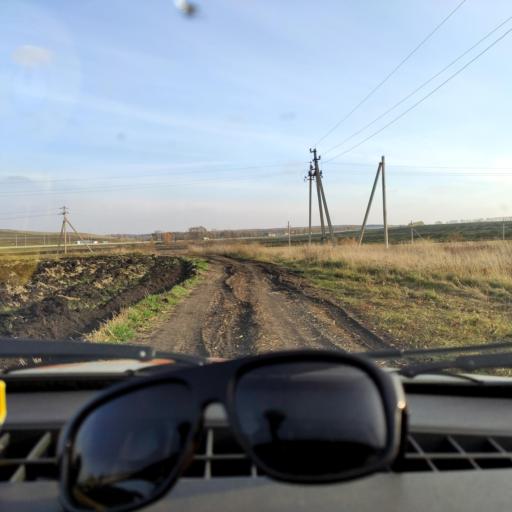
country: RU
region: Bashkortostan
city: Tolbazy
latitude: 53.9574
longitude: 55.9086
